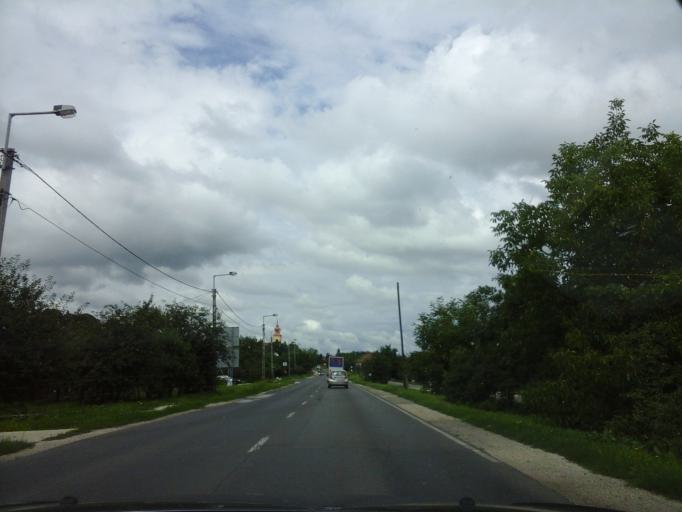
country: HU
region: Borsod-Abauj-Zemplen
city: Sajoszentpeter
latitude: 48.2107
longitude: 20.7313
